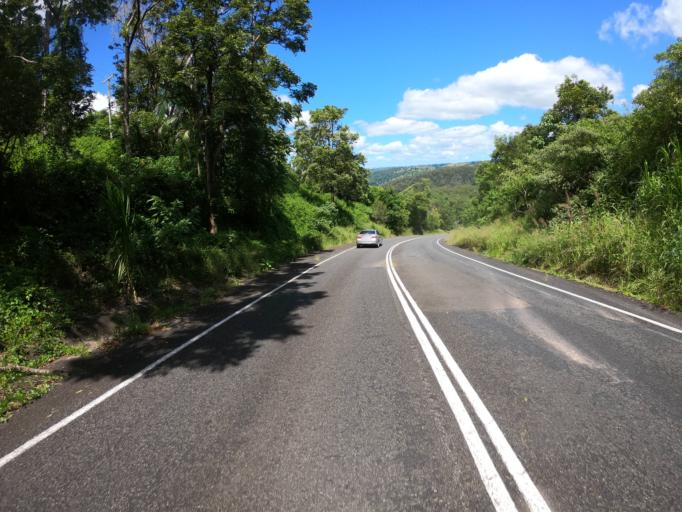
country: AU
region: Queensland
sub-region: Moreton Bay
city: Burpengary
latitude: -27.1504
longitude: 152.9812
